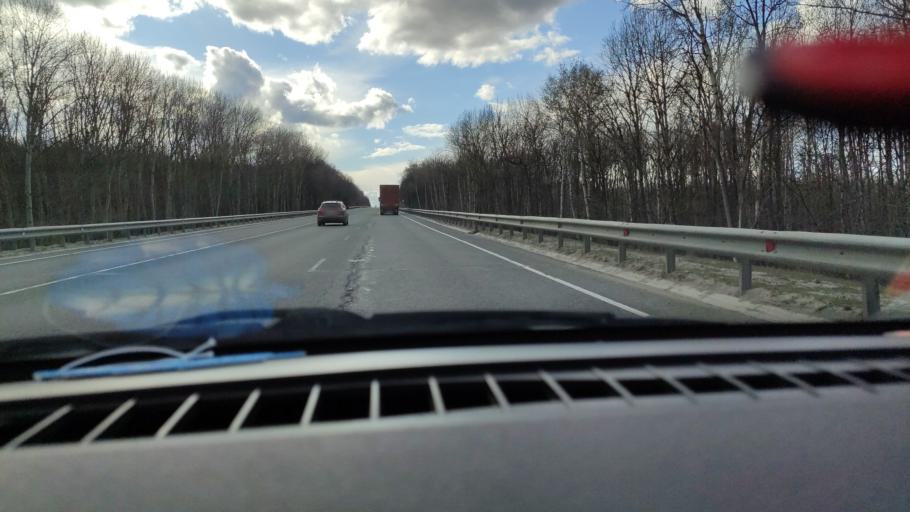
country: RU
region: Saratov
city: Vol'sk
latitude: 52.1072
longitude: 47.4106
